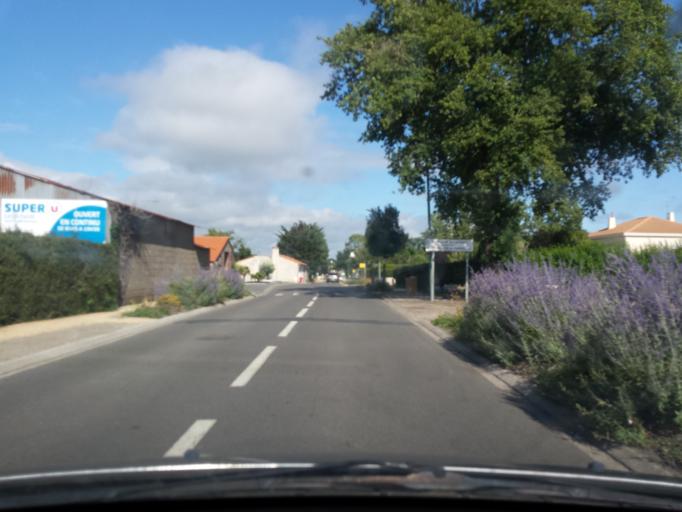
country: FR
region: Pays de la Loire
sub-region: Departement de la Vendee
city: Saint-Julien-des-Landes
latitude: 46.6413
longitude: -1.7206
